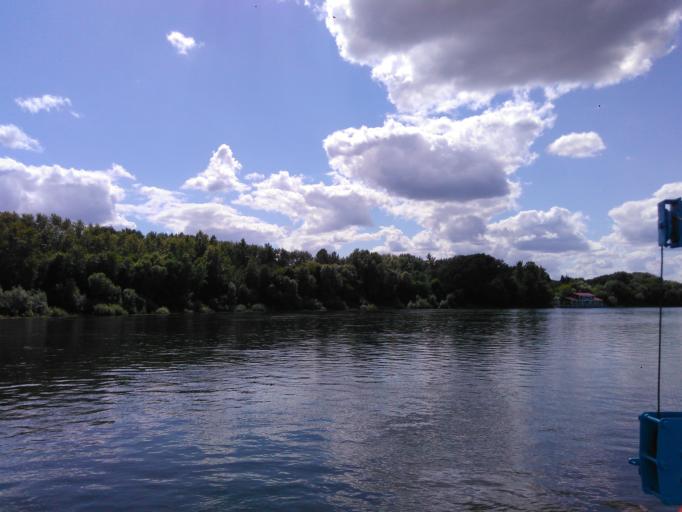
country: RU
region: Rjazan
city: Polyany
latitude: 54.6506
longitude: 39.7771
